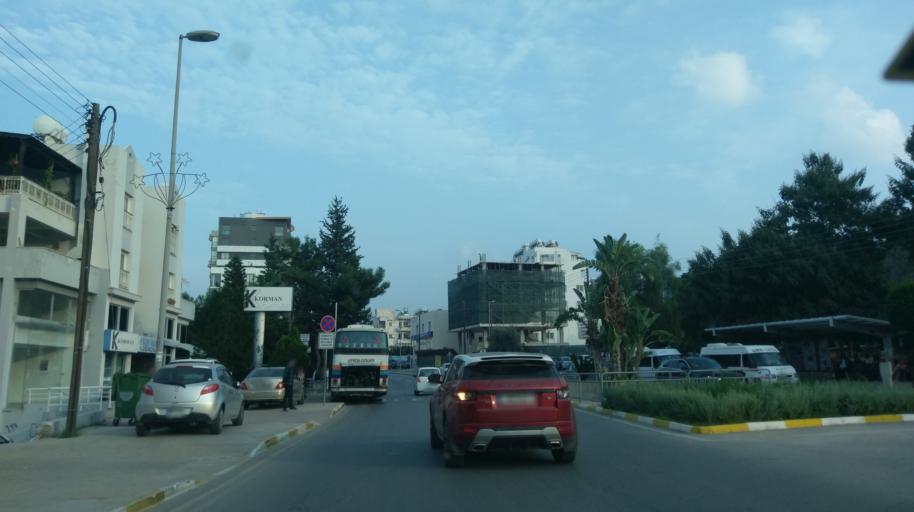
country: CY
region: Keryneia
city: Kyrenia
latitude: 35.3329
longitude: 33.3140
